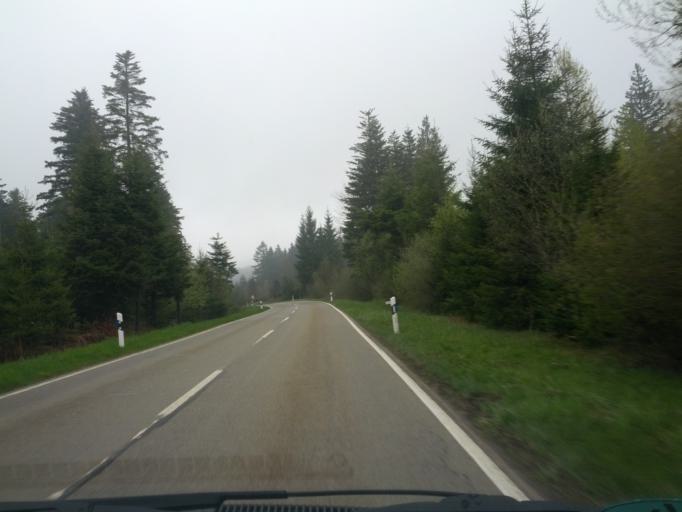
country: DE
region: Baden-Wuerttemberg
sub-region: Freiburg Region
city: Rickenbach
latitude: 47.6066
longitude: 8.0160
